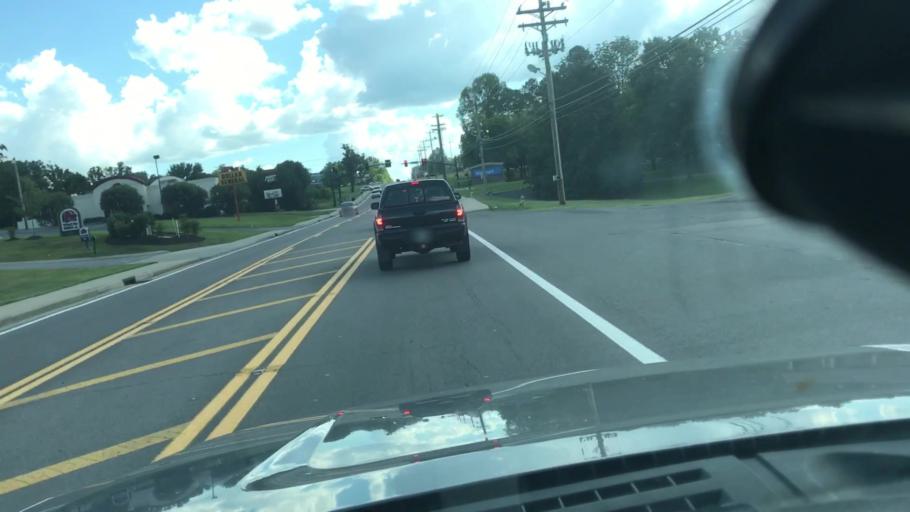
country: US
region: Tennessee
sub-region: Williamson County
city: Fairview
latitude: 35.9631
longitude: -87.1351
